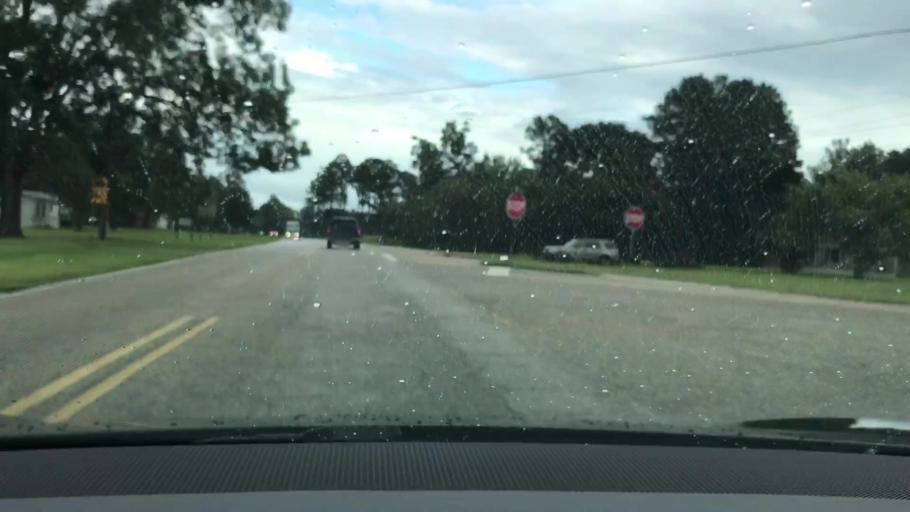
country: US
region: Alabama
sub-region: Geneva County
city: Samson
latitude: 31.1167
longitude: -86.1203
